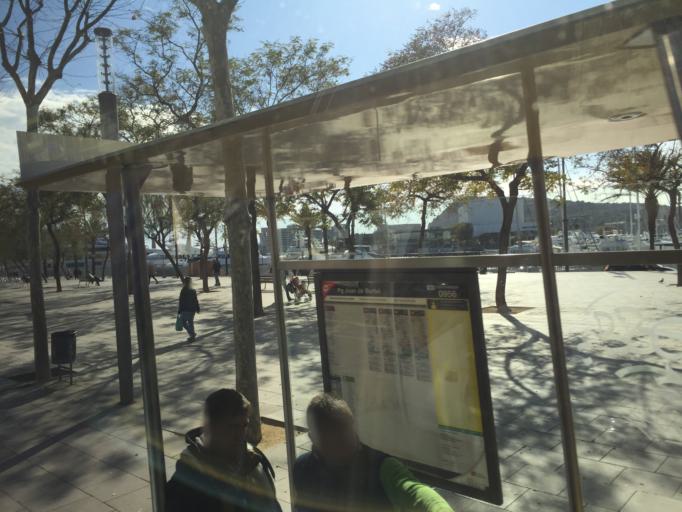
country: ES
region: Catalonia
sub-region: Provincia de Barcelona
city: Ciutat Vella
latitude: 41.3799
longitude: 2.1873
